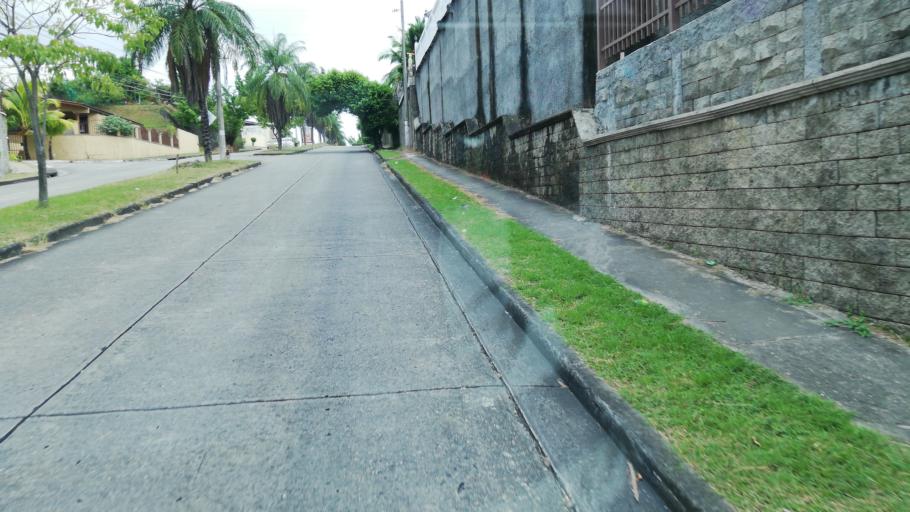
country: PA
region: Panama
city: San Miguelito
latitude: 9.0638
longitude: -79.4590
